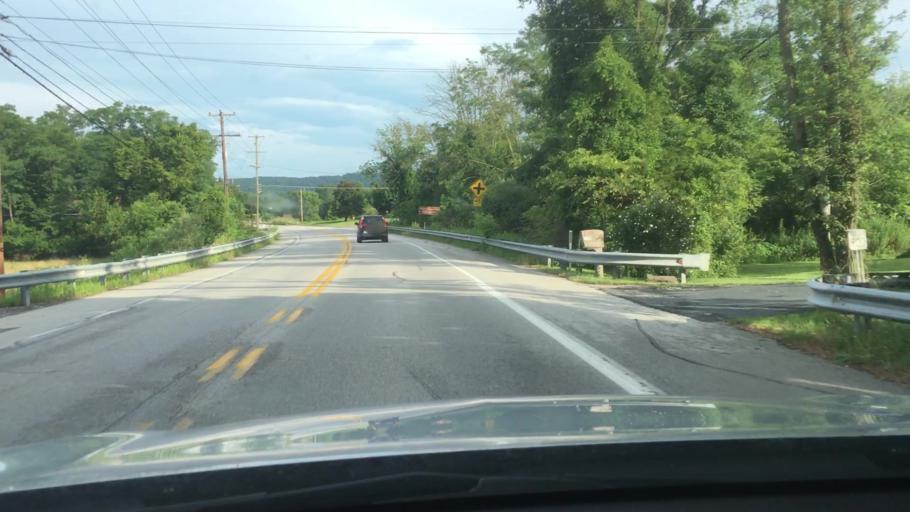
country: US
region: Pennsylvania
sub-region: York County
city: Dover
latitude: 40.0554
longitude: -76.9114
